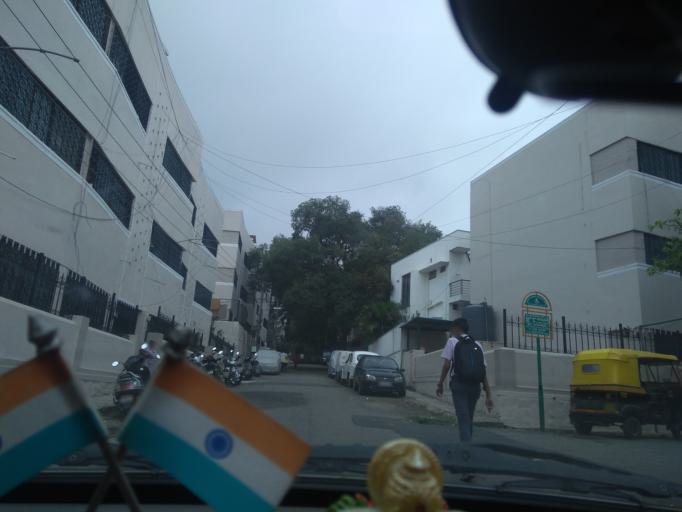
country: IN
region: Karnataka
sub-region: Bangalore Urban
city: Bangalore
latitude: 12.9755
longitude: 77.5515
